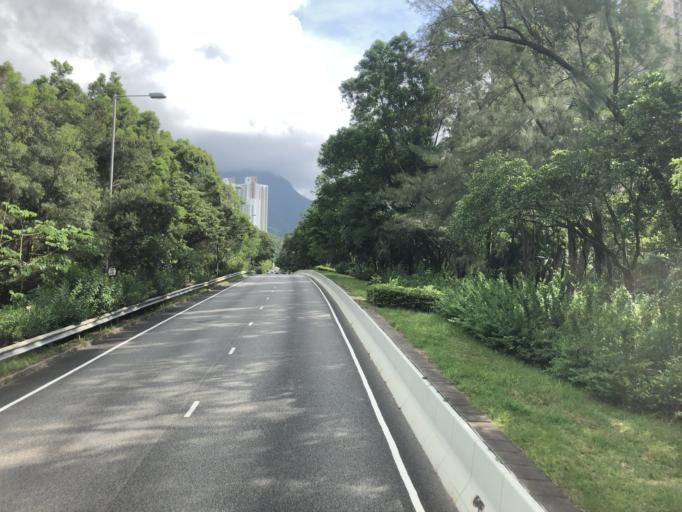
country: HK
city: Tai O
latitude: 22.2868
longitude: 113.9448
